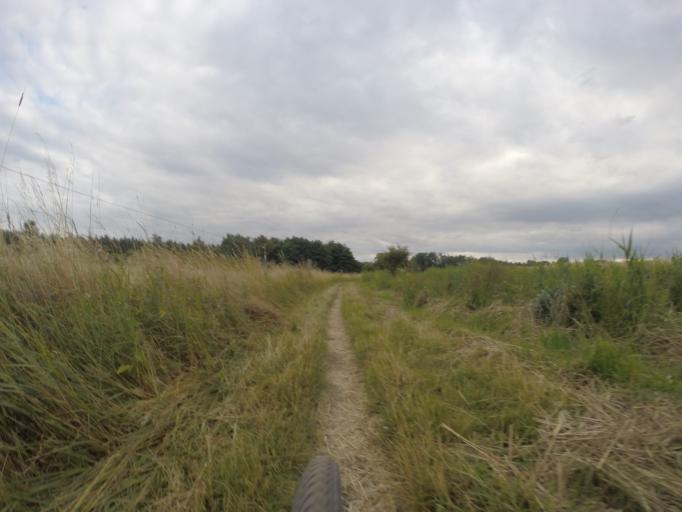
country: DK
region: Capital Region
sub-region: Ballerup Kommune
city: Ballerup
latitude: 55.7055
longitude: 12.3402
